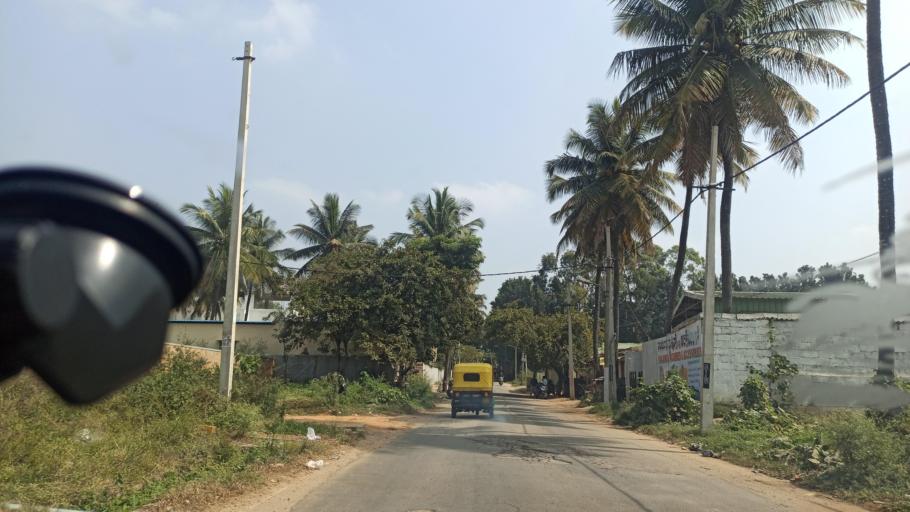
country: IN
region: Karnataka
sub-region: Bangalore Urban
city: Yelahanka
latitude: 13.0806
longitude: 77.6153
